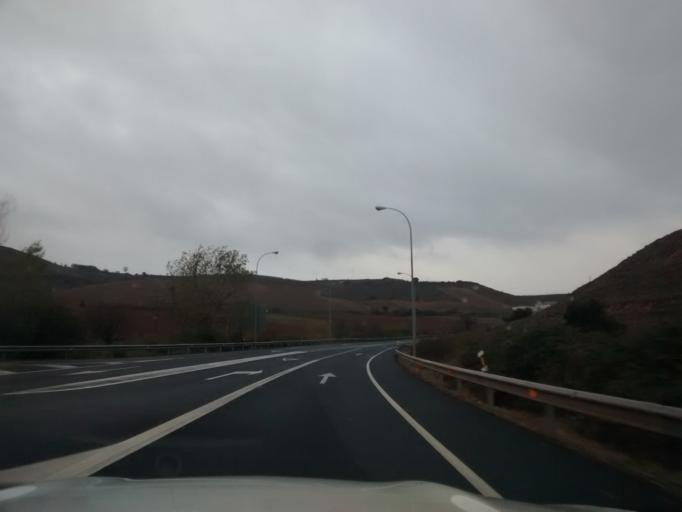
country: ES
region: La Rioja
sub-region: Provincia de La Rioja
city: Cenicero
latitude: 42.4715
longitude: -2.6401
